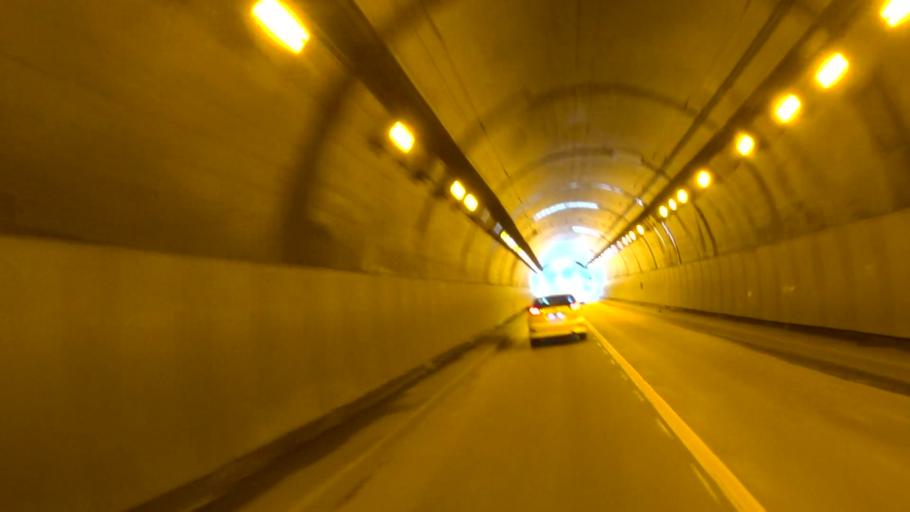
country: JP
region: Kyoto
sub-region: Kyoto-shi
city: Kamigyo-ku
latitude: 35.1144
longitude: 135.6649
